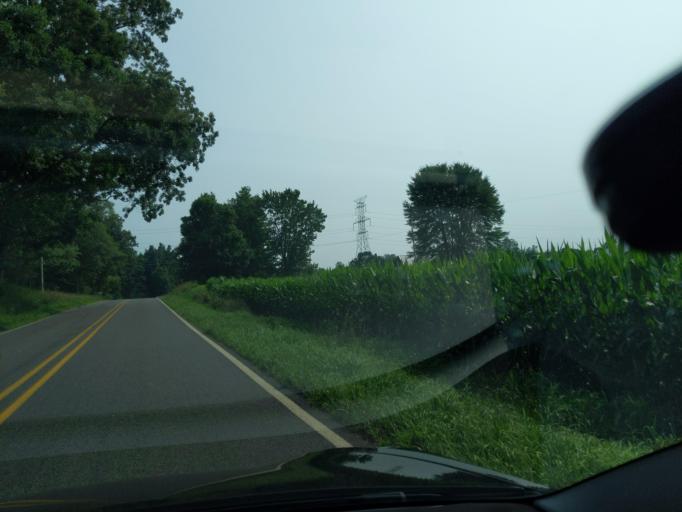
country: US
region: Michigan
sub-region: Eaton County
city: Eaton Rapids
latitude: 42.4171
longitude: -84.5611
